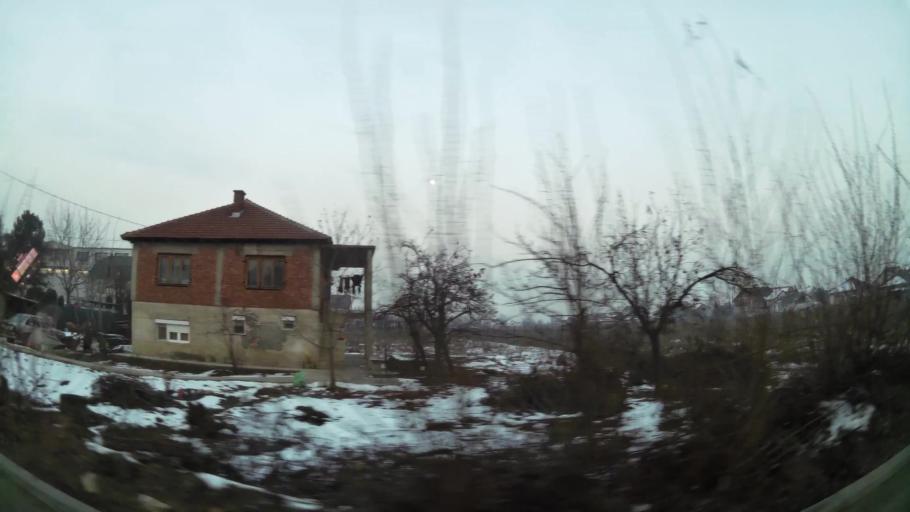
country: MK
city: Creshevo
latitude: 42.0124
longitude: 21.5166
